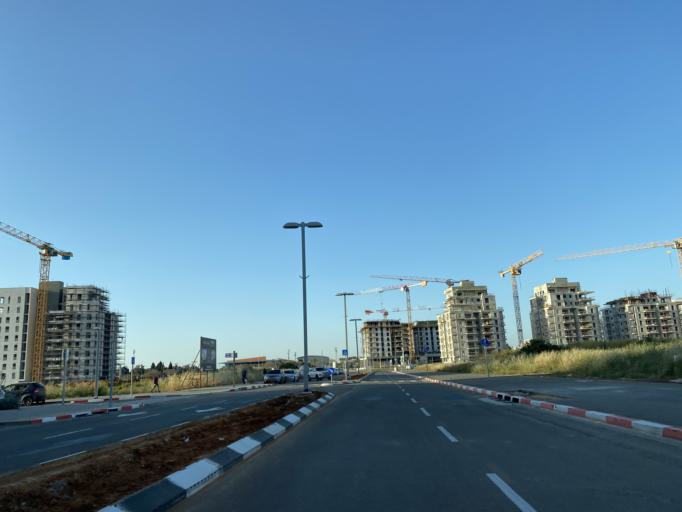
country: IL
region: Tel Aviv
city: Herzliyya
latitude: 32.1590
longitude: 34.8232
